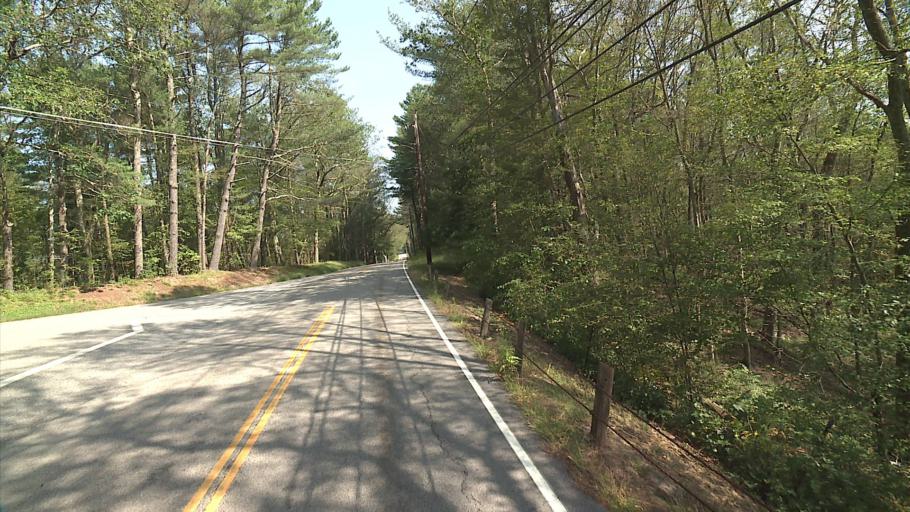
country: US
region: Connecticut
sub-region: Windham County
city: Wauregan
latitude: 41.7711
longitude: -71.9549
